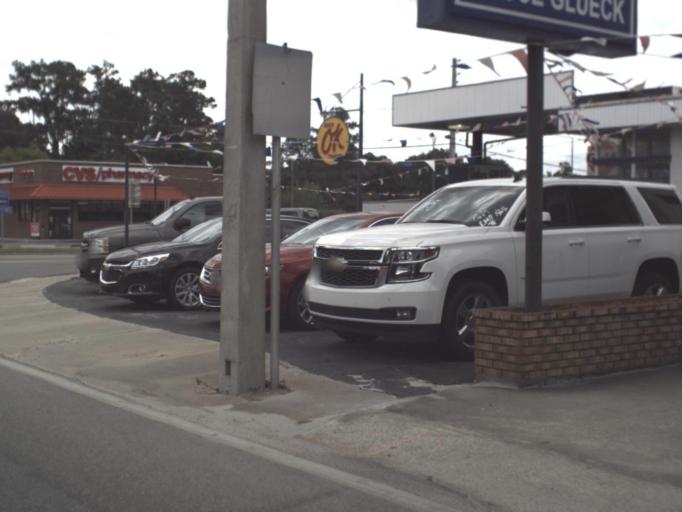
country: US
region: Florida
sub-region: Hamilton County
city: Jasper
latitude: 30.5180
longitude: -82.9462
